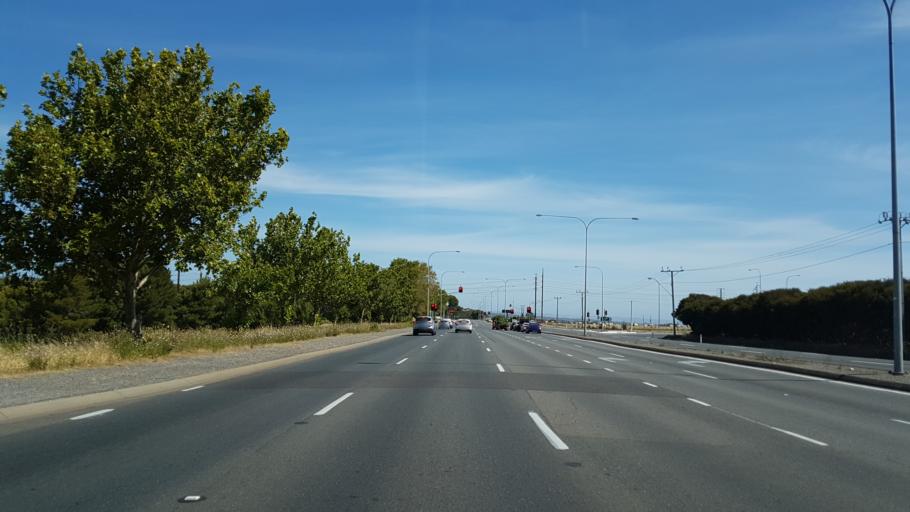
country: AU
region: South Australia
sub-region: Onkaparinga
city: Bedford Park
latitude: -35.0523
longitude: 138.5596
